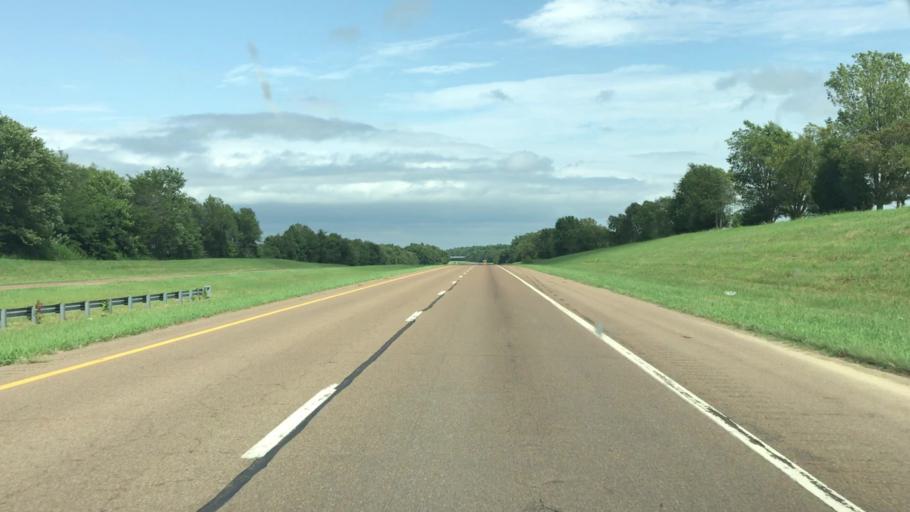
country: US
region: Tennessee
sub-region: Obion County
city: South Fulton
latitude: 36.4764
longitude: -88.9562
